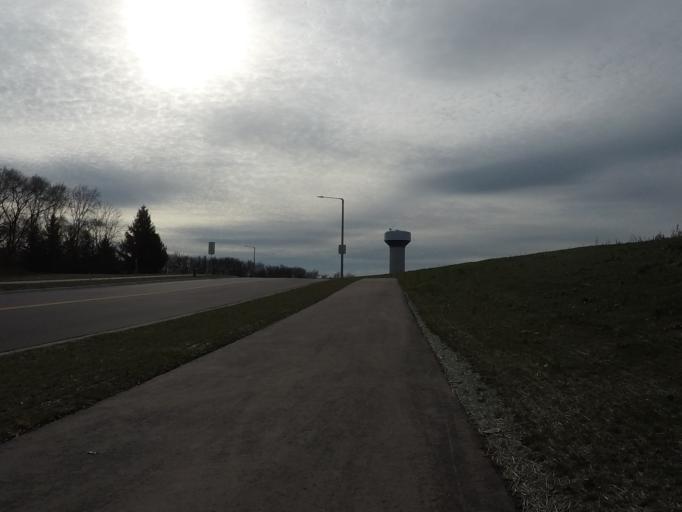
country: US
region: Wisconsin
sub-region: Dane County
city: Middleton
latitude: 43.0767
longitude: -89.5630
